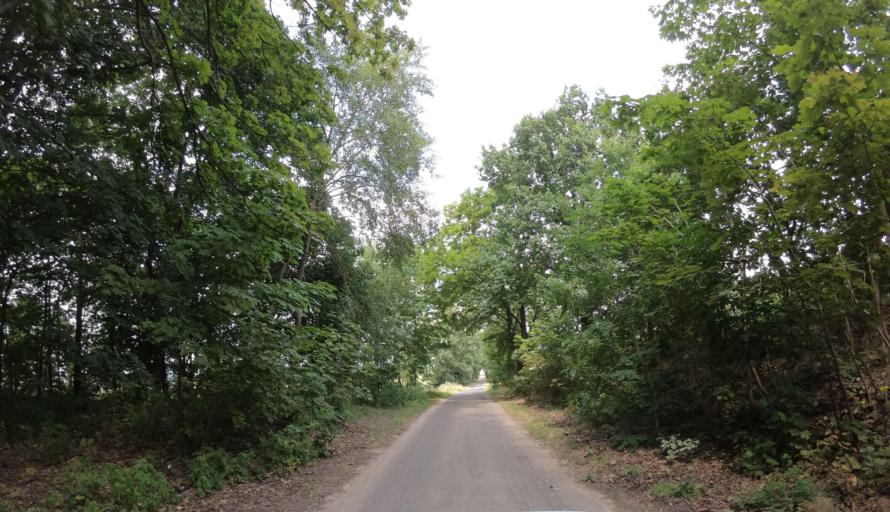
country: PL
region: West Pomeranian Voivodeship
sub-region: Powiat stargardzki
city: Kobylanka
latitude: 53.3118
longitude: 14.8313
